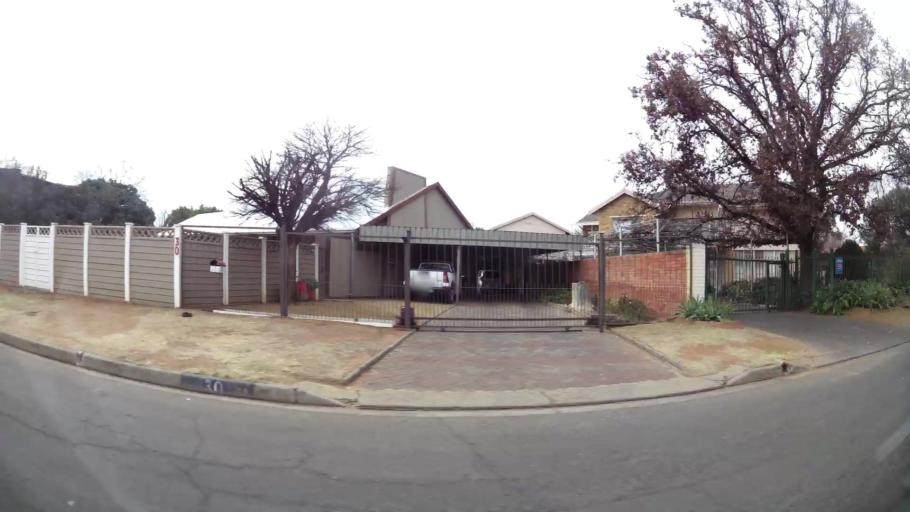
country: ZA
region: Orange Free State
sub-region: Mangaung Metropolitan Municipality
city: Bloemfontein
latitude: -29.1224
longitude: 26.1940
